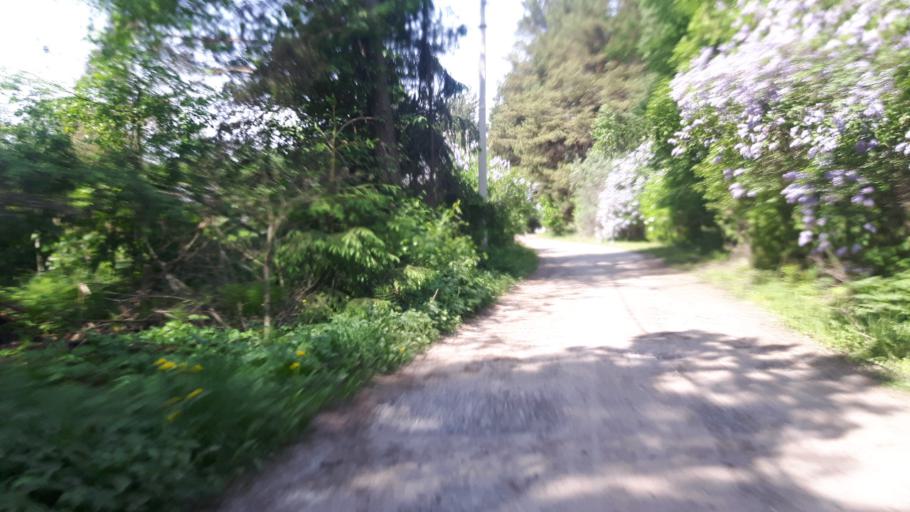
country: RU
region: Leningrad
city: Vistino
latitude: 59.6749
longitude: 28.4424
